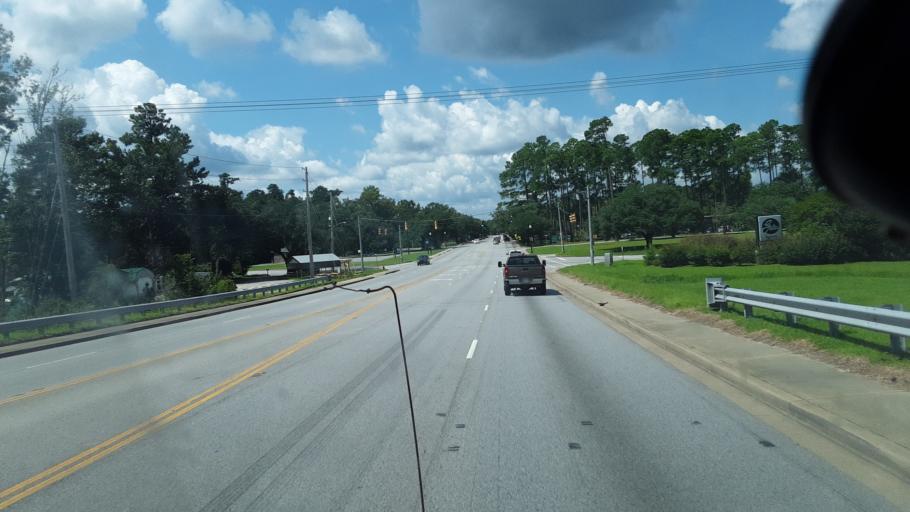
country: US
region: South Carolina
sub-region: Berkeley County
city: Moncks Corner
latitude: 33.1992
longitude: -80.0032
